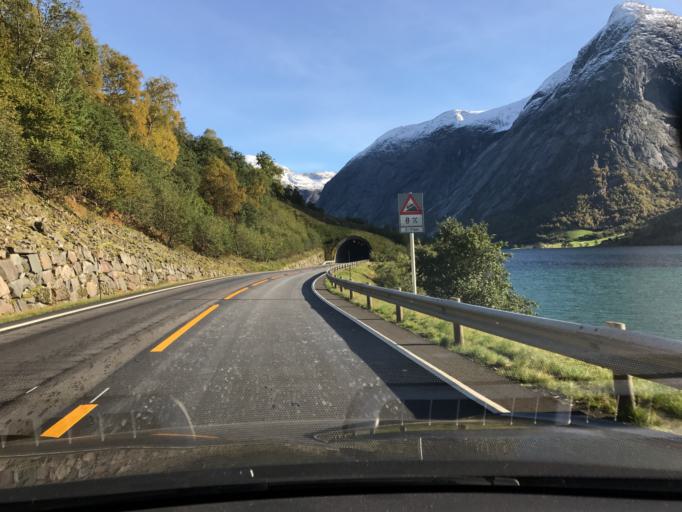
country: NO
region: Sogn og Fjordane
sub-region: Jolster
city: Skei
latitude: 61.5333
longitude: 6.5633
